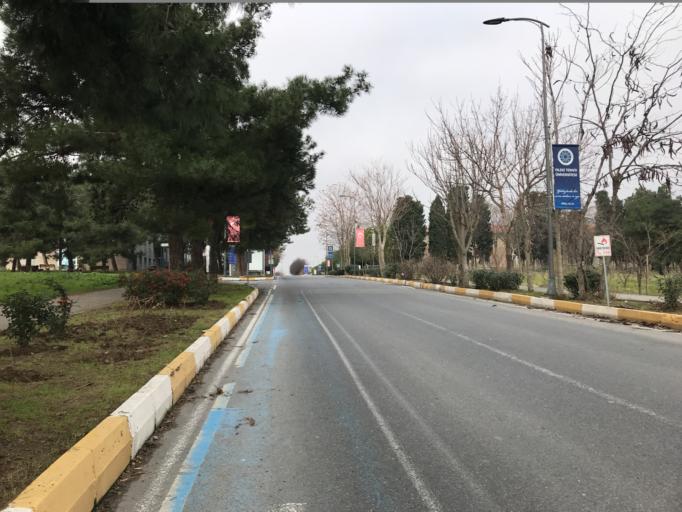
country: TR
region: Istanbul
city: merter keresteciler
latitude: 41.0231
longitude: 28.8900
